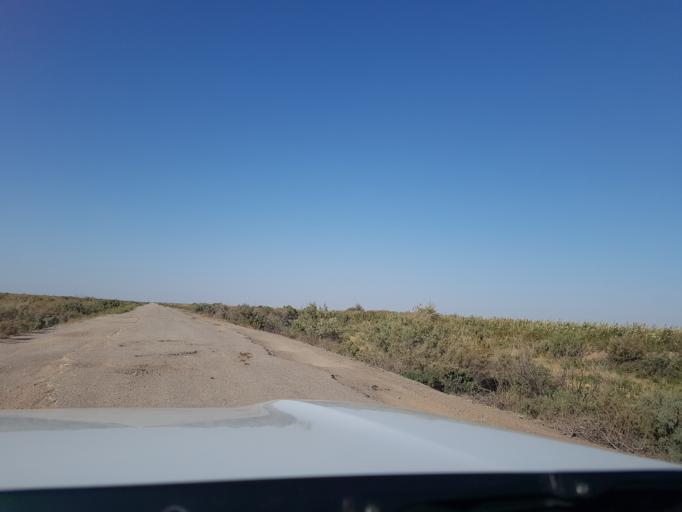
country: IR
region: Razavi Khorasan
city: Sarakhs
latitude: 36.9599
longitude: 61.3819
